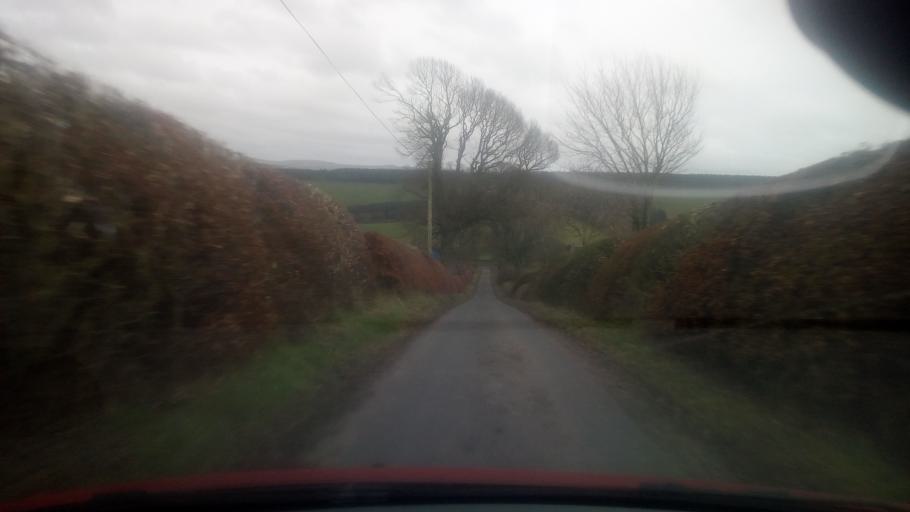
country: GB
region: Scotland
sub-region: The Scottish Borders
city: Jedburgh
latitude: 55.4612
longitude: -2.5158
